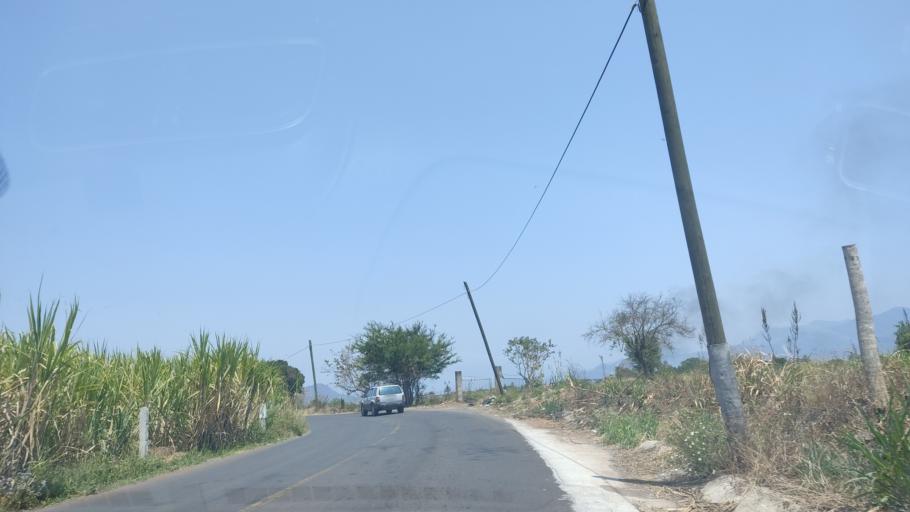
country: MX
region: Nayarit
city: Puga
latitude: 21.5729
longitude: -104.8254
